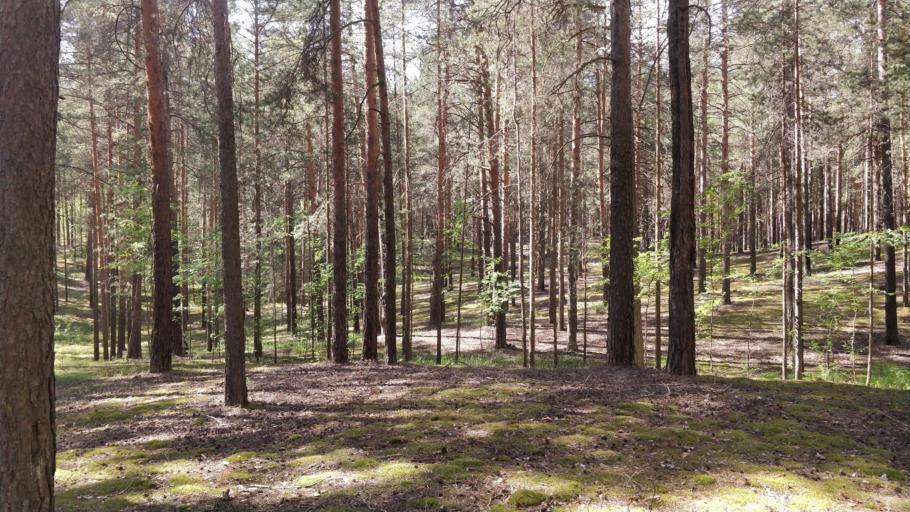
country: RU
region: Perm
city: Perm
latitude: 58.0725
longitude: 56.3047
